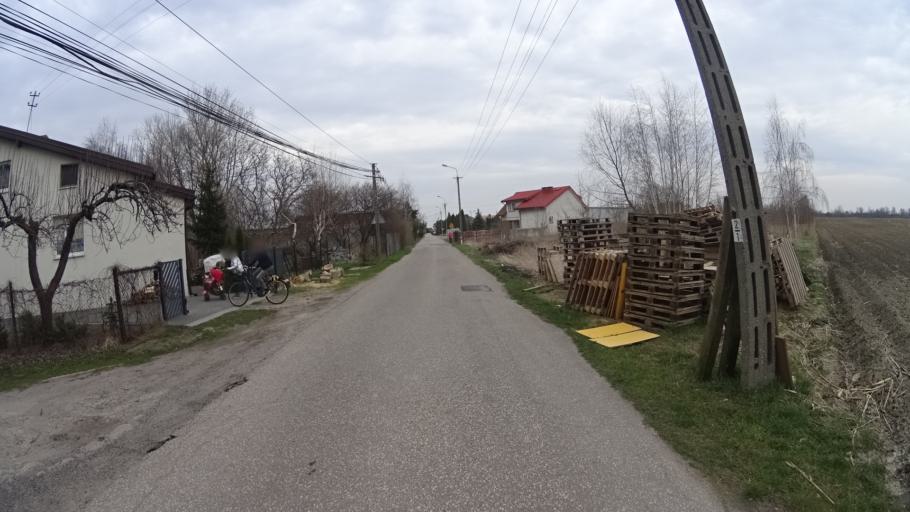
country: PL
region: Masovian Voivodeship
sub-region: Powiat warszawski zachodni
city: Jozefow
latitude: 52.2077
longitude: 20.6653
